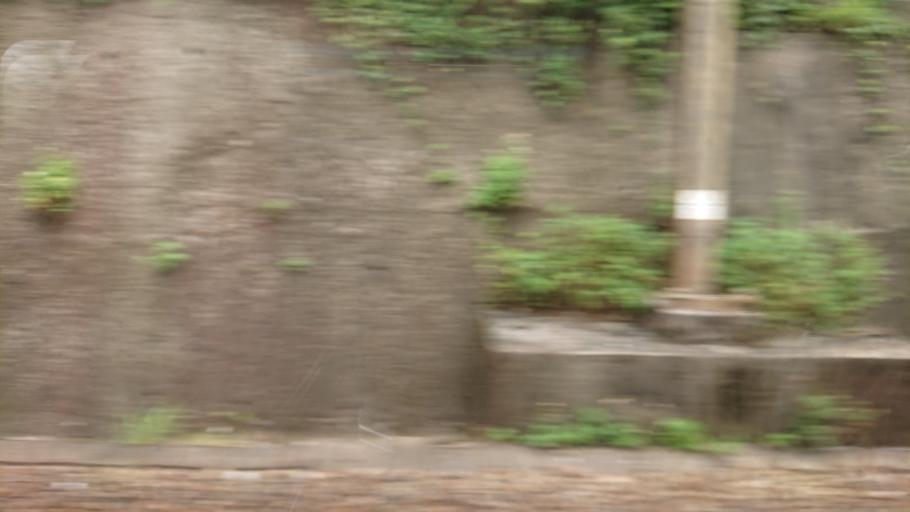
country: TW
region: Taiwan
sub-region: Keelung
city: Keelung
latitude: 24.9543
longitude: 121.9154
